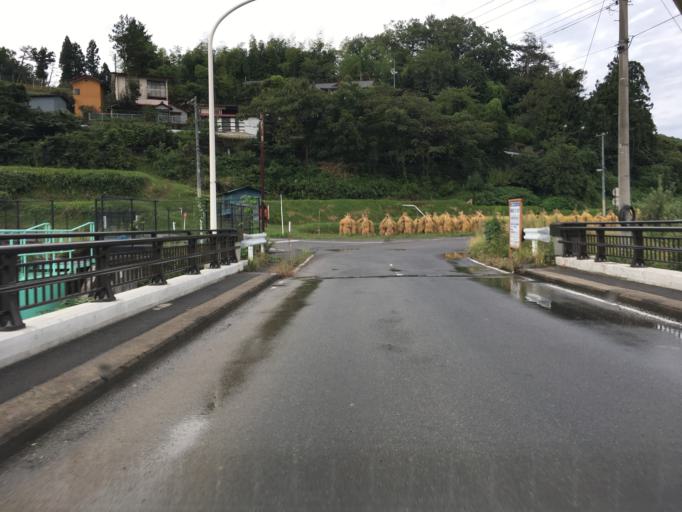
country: JP
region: Fukushima
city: Fukushima-shi
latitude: 37.8360
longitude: 140.4380
